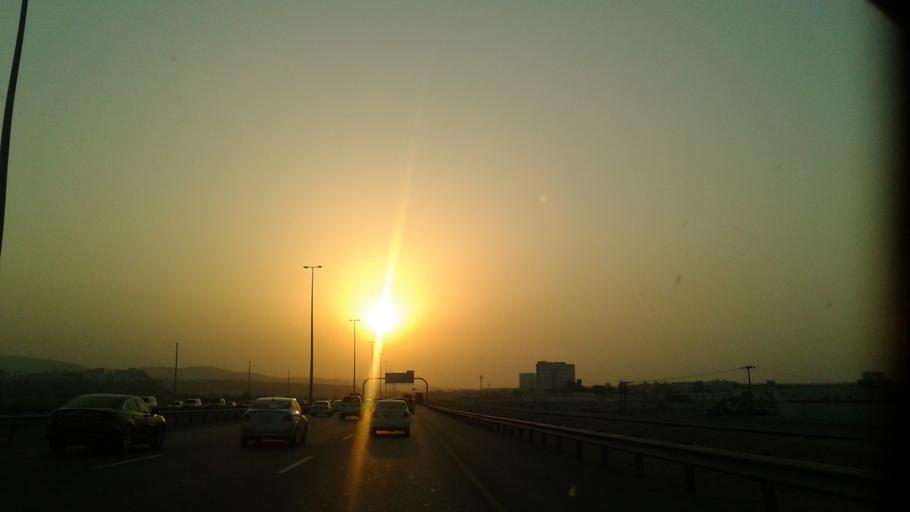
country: OM
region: Muhafazat Masqat
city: Bawshar
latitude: 23.5659
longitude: 58.3617
